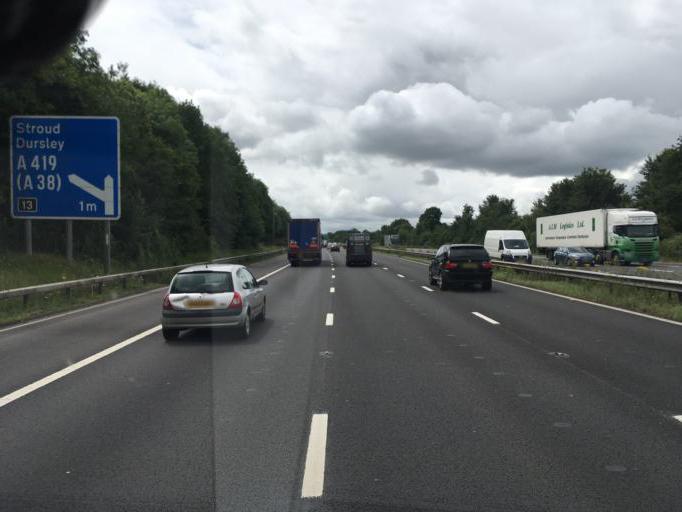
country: GB
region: England
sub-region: Gloucestershire
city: Stonehouse
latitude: 51.7773
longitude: -2.3089
